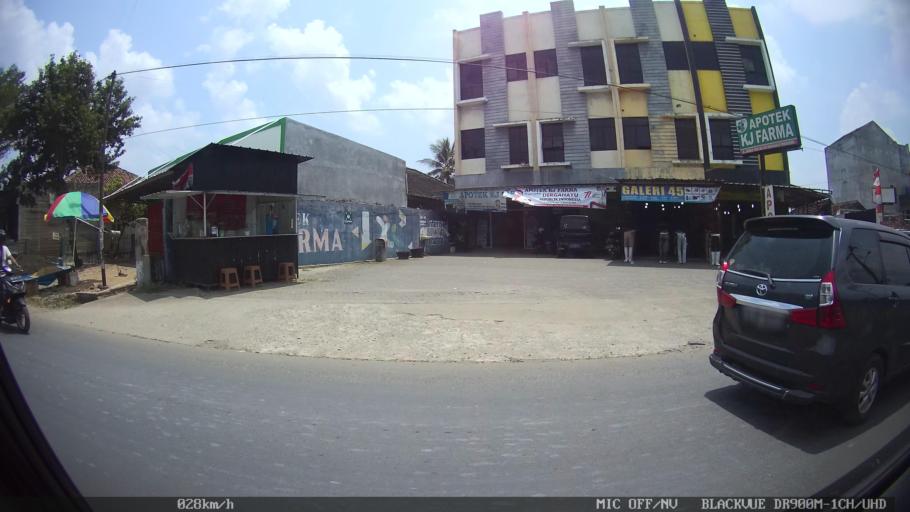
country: ID
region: Lampung
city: Pringsewu
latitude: -5.3585
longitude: 104.9896
